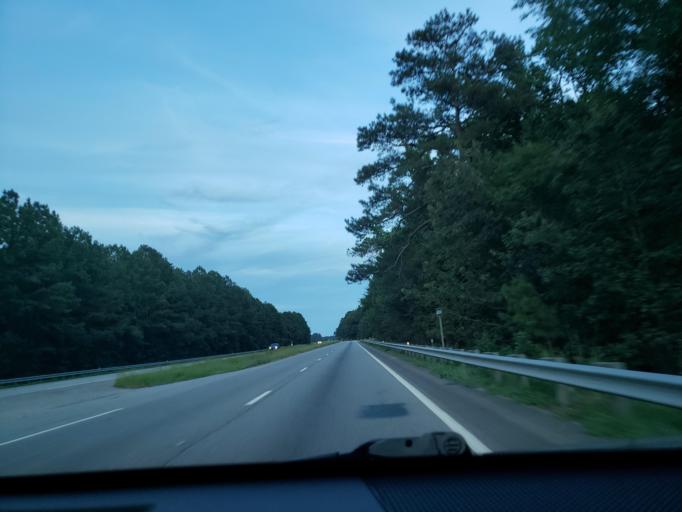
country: US
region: Virginia
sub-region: Southampton County
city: Courtland
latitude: 36.7074
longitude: -77.1557
